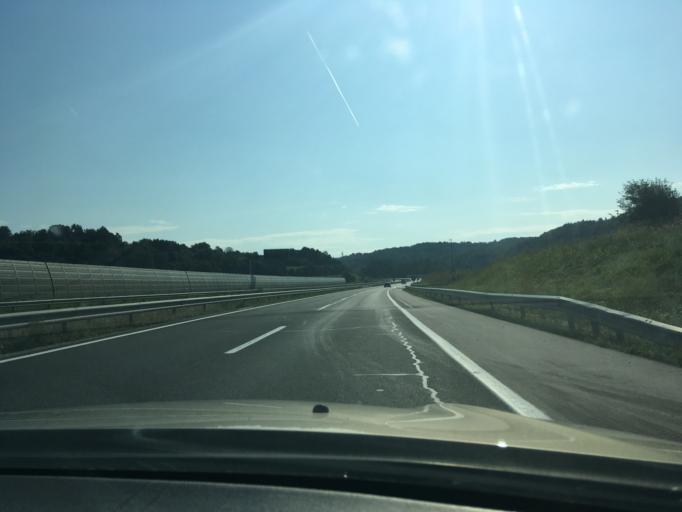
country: SI
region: Ivancna Gorica
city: Sentvid pri Sticni
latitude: 45.9233
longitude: 14.8891
